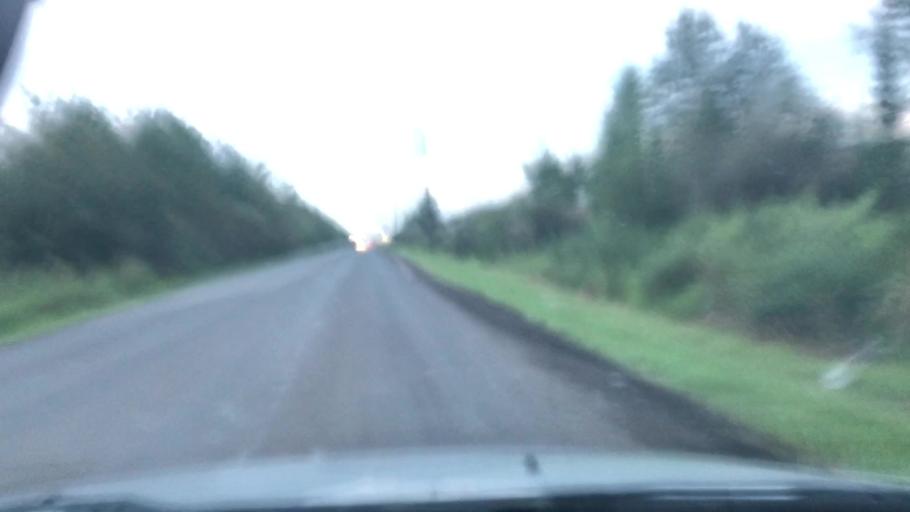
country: CA
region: Alberta
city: Devon
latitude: 53.4930
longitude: -113.6889
